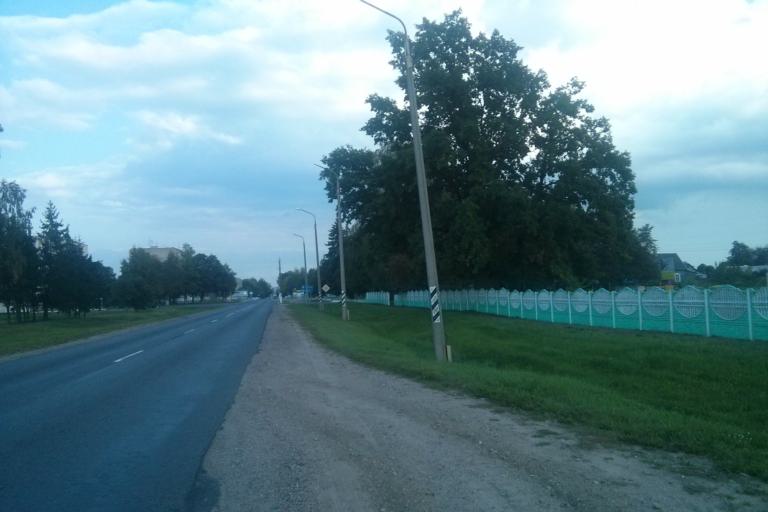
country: BY
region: Minsk
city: Chervyen'
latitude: 53.7201
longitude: 28.3946
